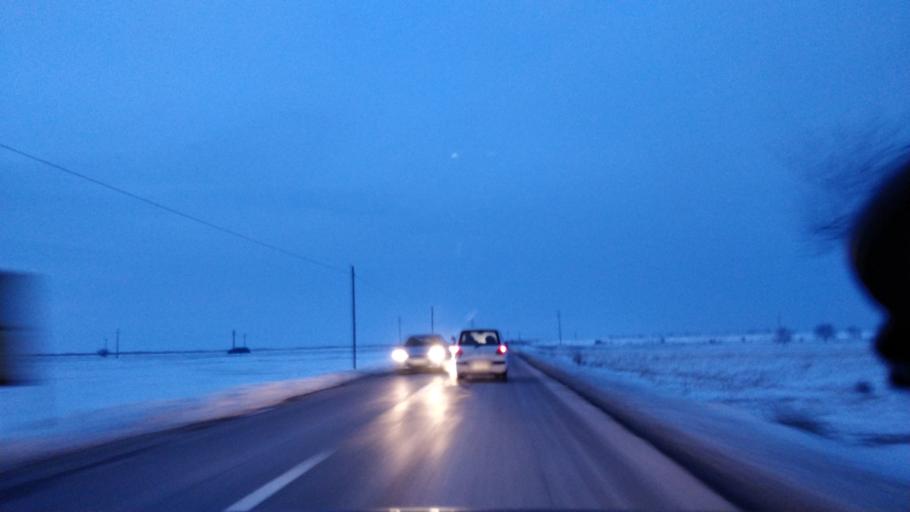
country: RO
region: Vrancea
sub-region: Comuna Nanesti
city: Nanesti
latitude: 45.5553
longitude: 27.5000
